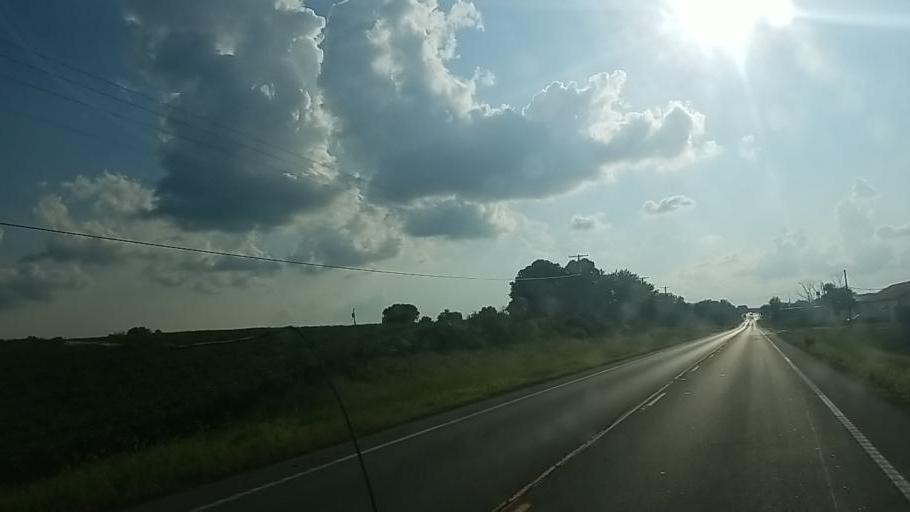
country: US
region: Ohio
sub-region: Ashland County
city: Ashland
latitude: 40.8573
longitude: -82.2418
